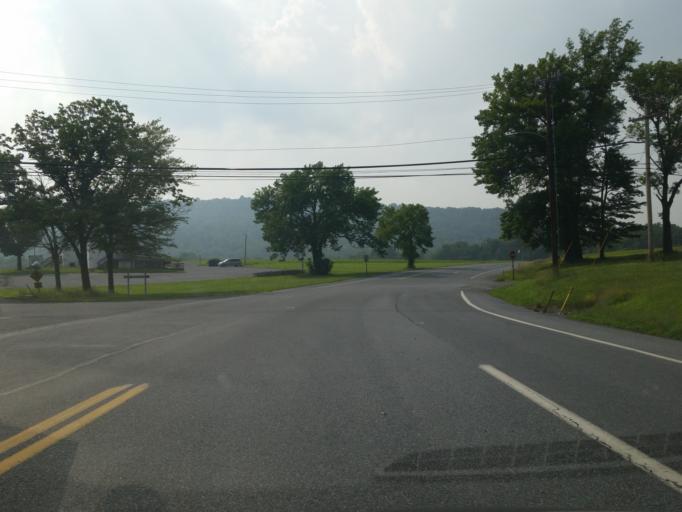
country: US
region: Pennsylvania
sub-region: Lebanon County
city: Jonestown
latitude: 40.4286
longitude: -76.5901
